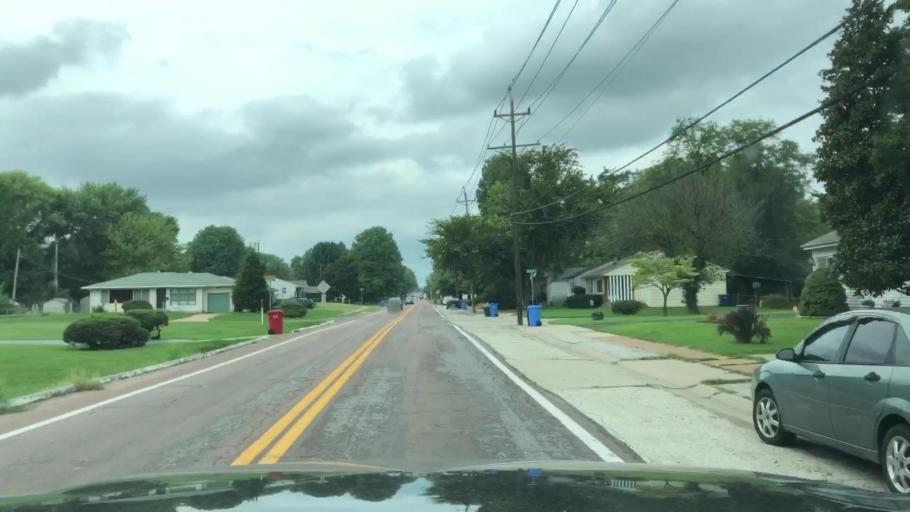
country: US
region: Missouri
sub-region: Saint Louis County
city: Florissant
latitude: 38.8022
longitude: -90.3475
